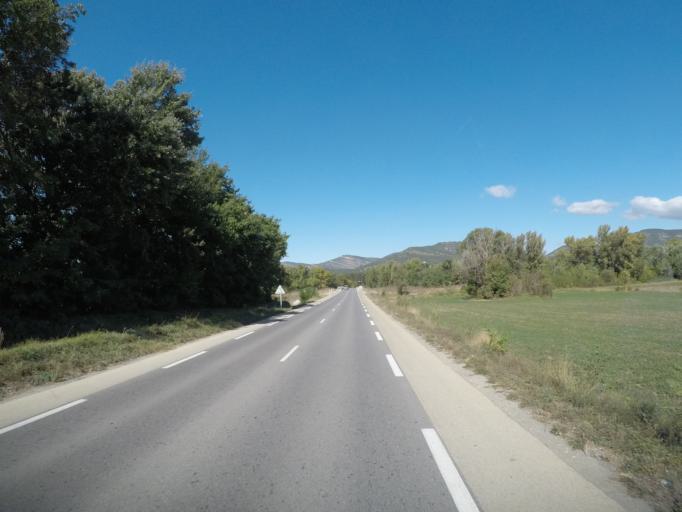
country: FR
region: Provence-Alpes-Cote d'Azur
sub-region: Departement des Alpes-de-Haute-Provence
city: Mallemoisson
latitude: 44.0384
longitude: 6.1450
